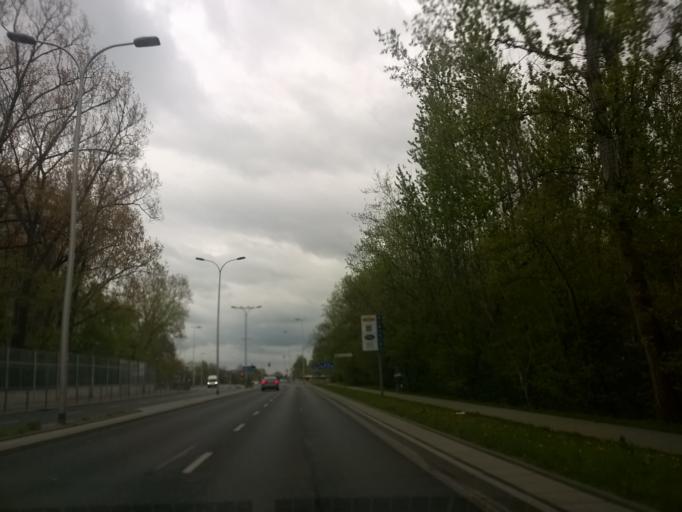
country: PL
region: Masovian Voivodeship
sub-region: Warszawa
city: Wilanow
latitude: 52.1703
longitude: 21.0650
